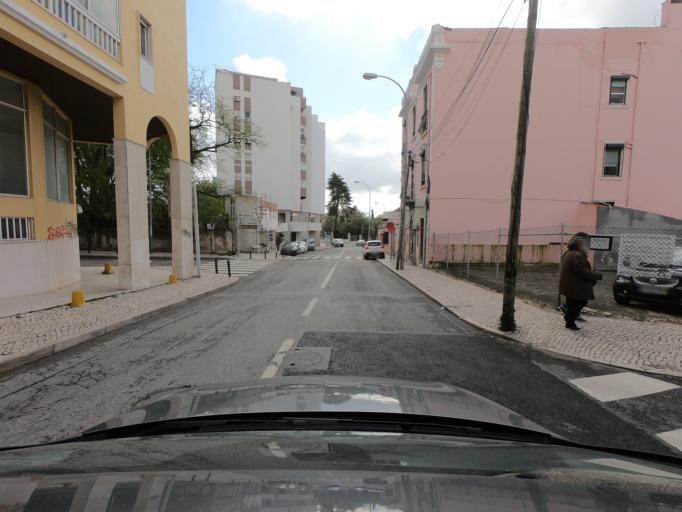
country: PT
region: Lisbon
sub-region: Oeiras
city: Alges
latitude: 38.7003
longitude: -9.2330
